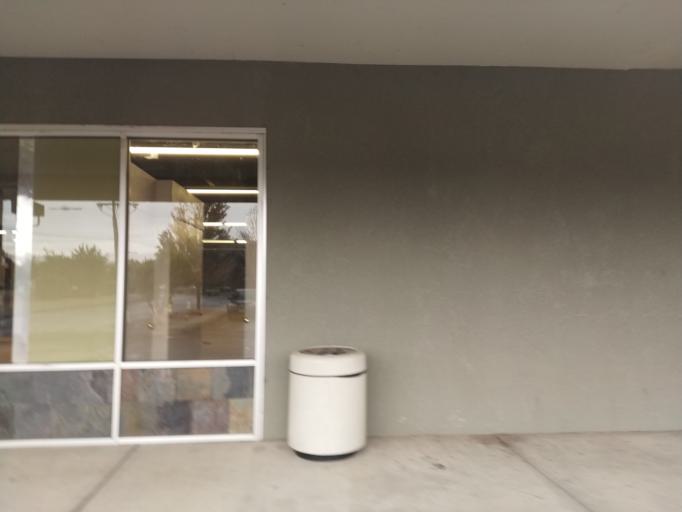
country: US
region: Colorado
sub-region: Mesa County
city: Grand Junction
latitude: 39.0787
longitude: -108.5342
